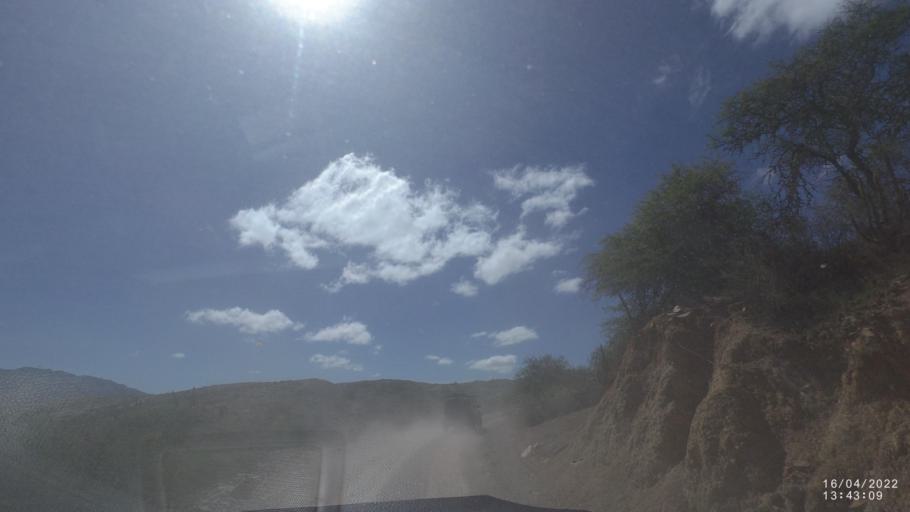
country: BO
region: Cochabamba
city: Mizque
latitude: -17.9981
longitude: -65.5938
